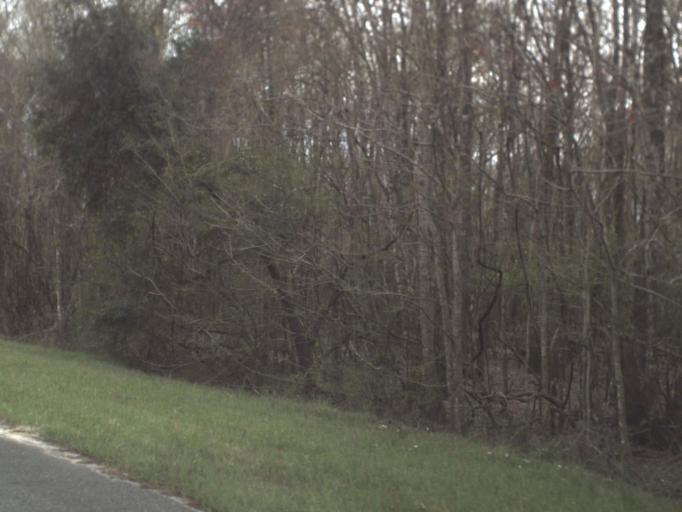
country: US
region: Florida
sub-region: Wakulla County
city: Crawfordville
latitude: 30.2462
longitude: -84.3168
